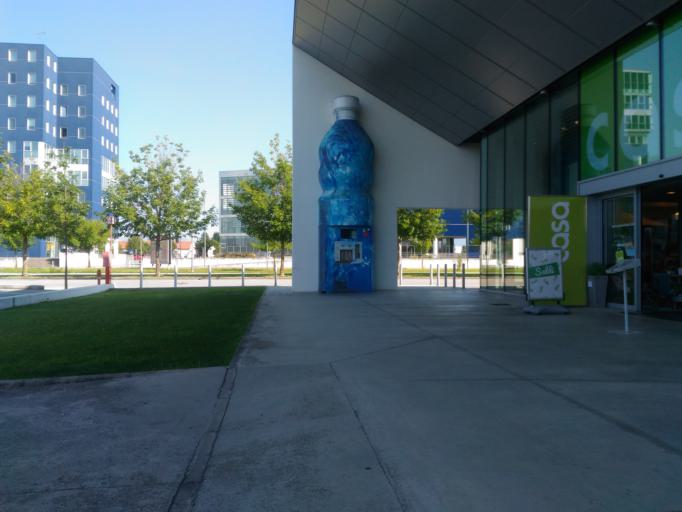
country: IT
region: Friuli Venezia Giulia
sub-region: Provincia di Udine
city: Feletto Umberto
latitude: 46.0949
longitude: 13.2341
